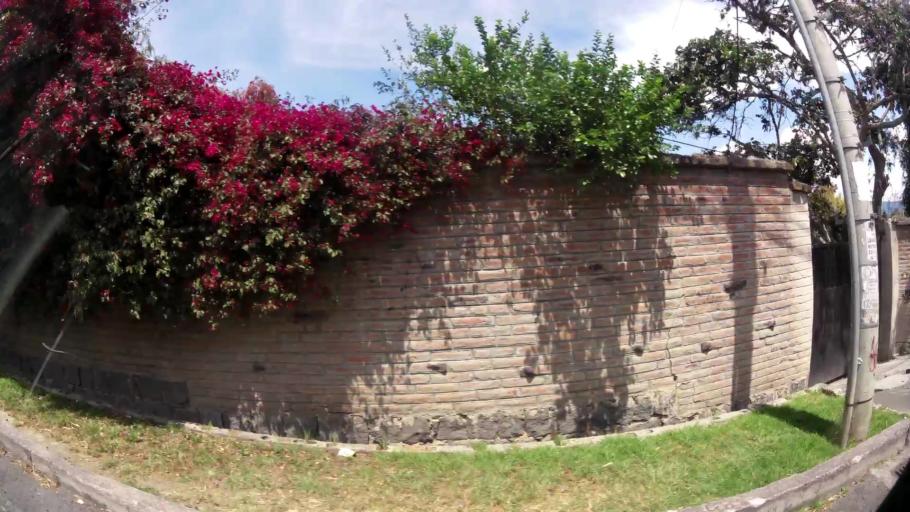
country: EC
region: Pichincha
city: Quito
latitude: -0.2142
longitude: -78.3926
